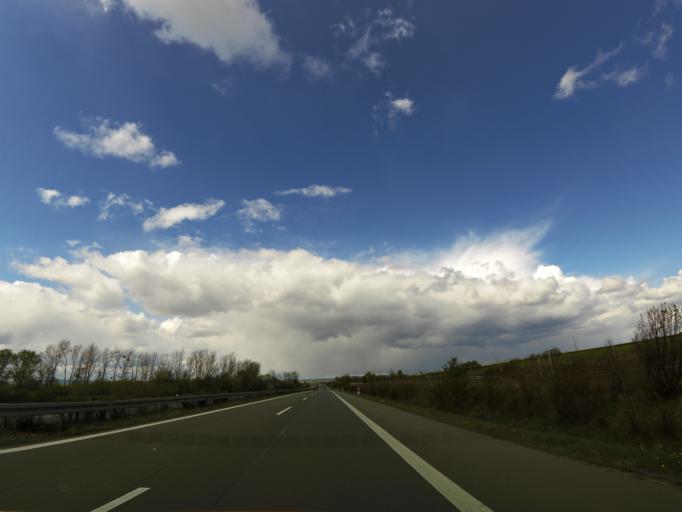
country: DE
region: Saxony-Anhalt
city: Stapelburg
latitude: 51.9214
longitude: 10.6586
